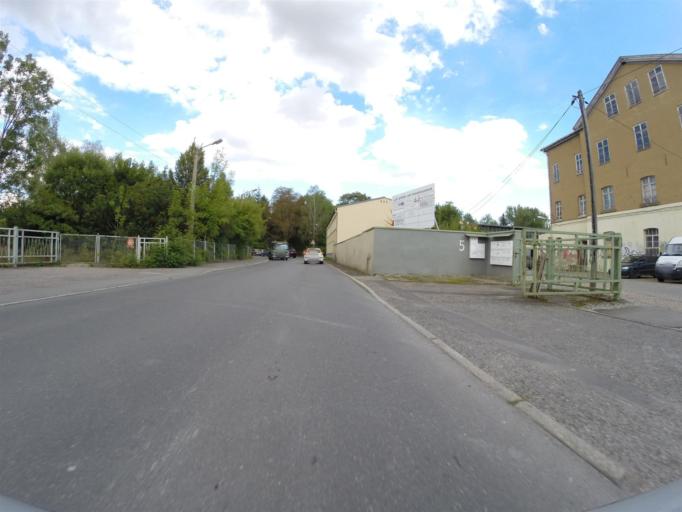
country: DE
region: Thuringia
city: Weimar
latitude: 50.9647
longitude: 11.3421
